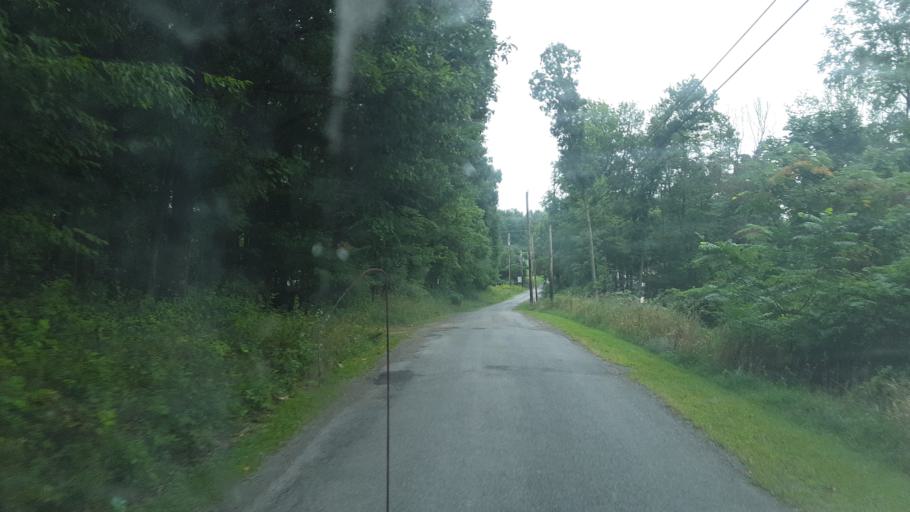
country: US
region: Pennsylvania
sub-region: Jefferson County
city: Punxsutawney
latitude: 40.9594
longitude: -79.1219
